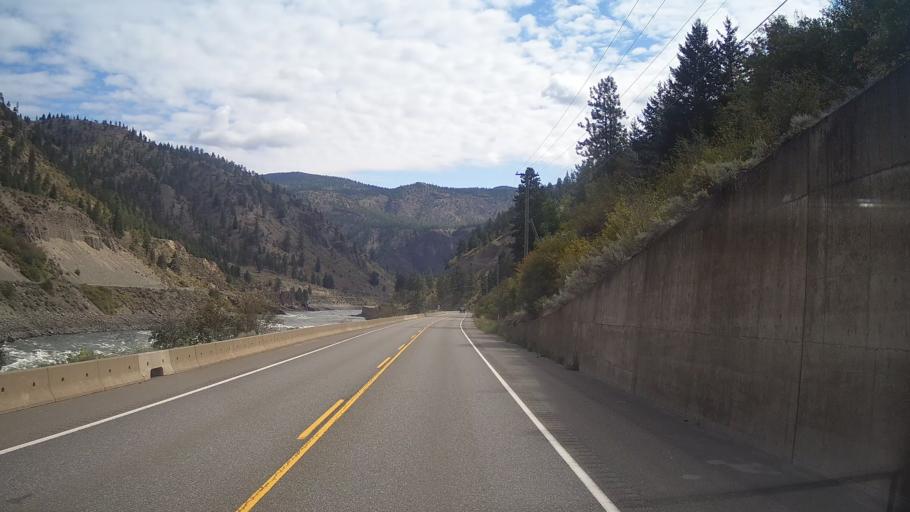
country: CA
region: British Columbia
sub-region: Thompson-Nicola Regional District
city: Ashcroft
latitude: 50.2600
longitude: -121.4264
